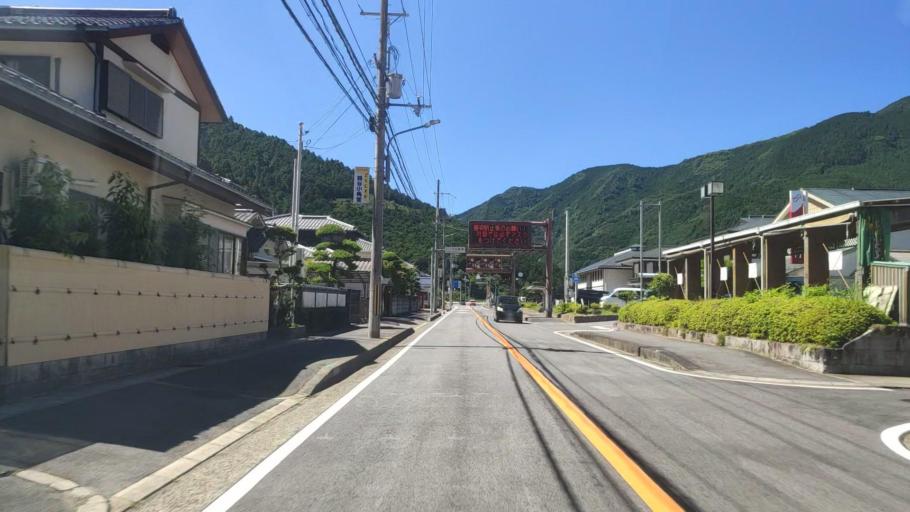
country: JP
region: Nara
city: Yoshino-cho
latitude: 34.3379
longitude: 135.9539
